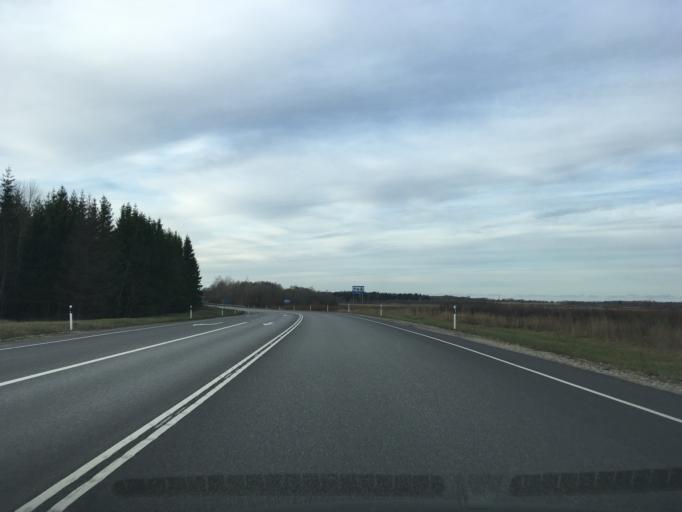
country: EE
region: Ida-Virumaa
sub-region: Narva-Joesuu linn
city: Narva-Joesuu
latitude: 59.3775
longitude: 27.9320
